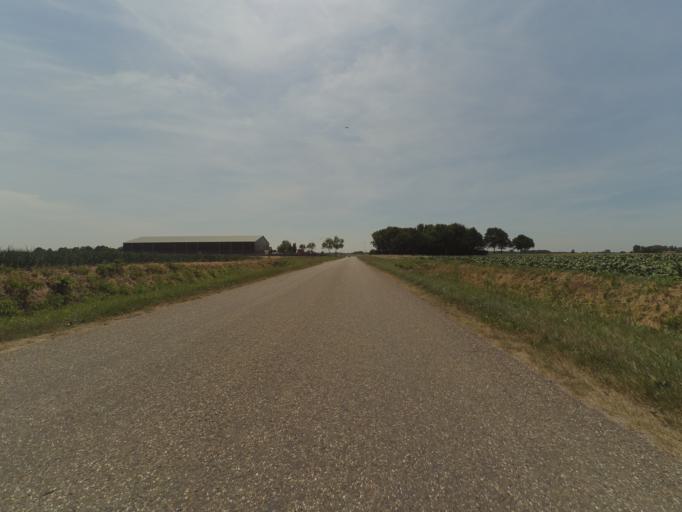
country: NL
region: North Brabant
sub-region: Gemeente Steenbergen
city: Kruisland
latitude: 51.5421
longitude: 4.3992
